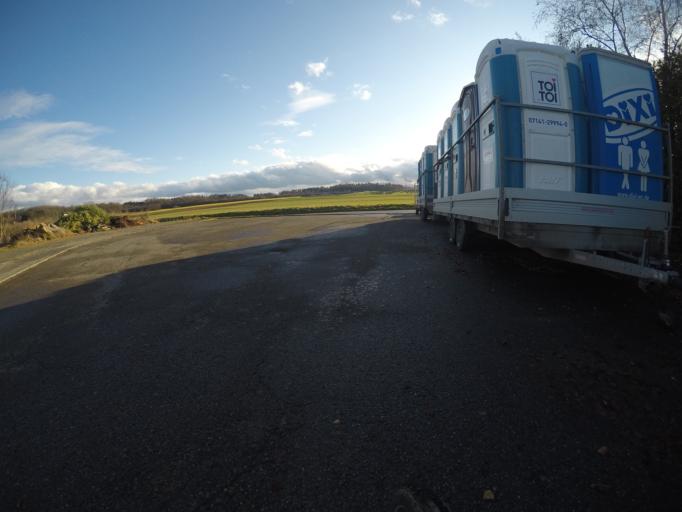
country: DE
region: Baden-Wuerttemberg
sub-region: Regierungsbezirk Stuttgart
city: Bondorf
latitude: 48.5274
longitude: 8.8760
